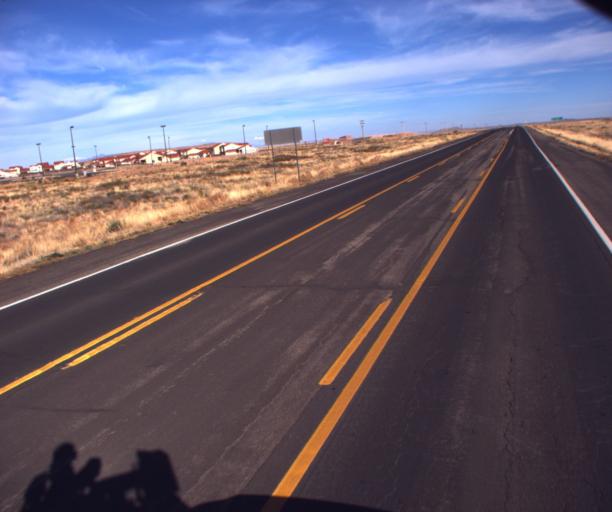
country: US
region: Arizona
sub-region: Apache County
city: Lukachukai
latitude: 36.9597
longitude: -109.3498
